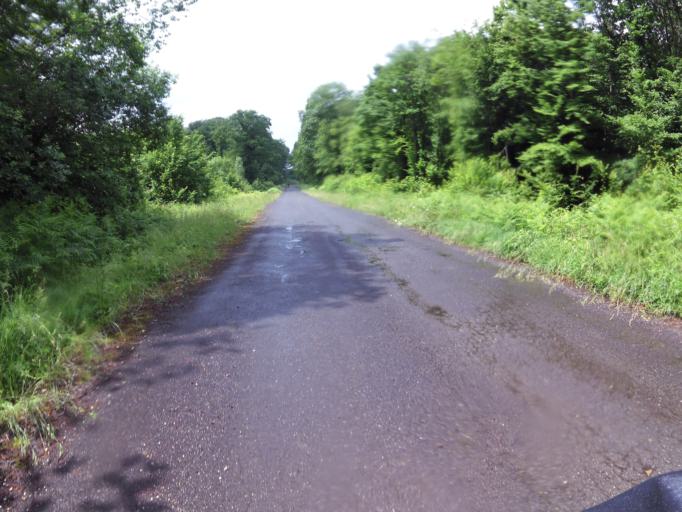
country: FR
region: Champagne-Ardenne
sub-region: Departement de la Marne
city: Sermaize-les-Bains
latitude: 48.7490
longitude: 4.9687
